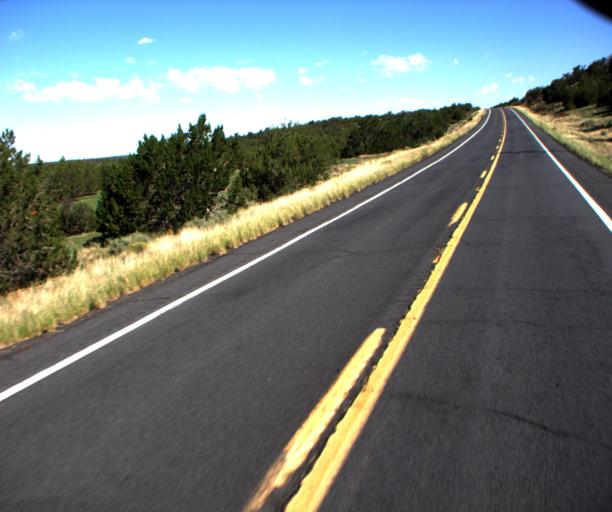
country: US
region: Arizona
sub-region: Coconino County
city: Williams
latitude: 35.4677
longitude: -112.1736
